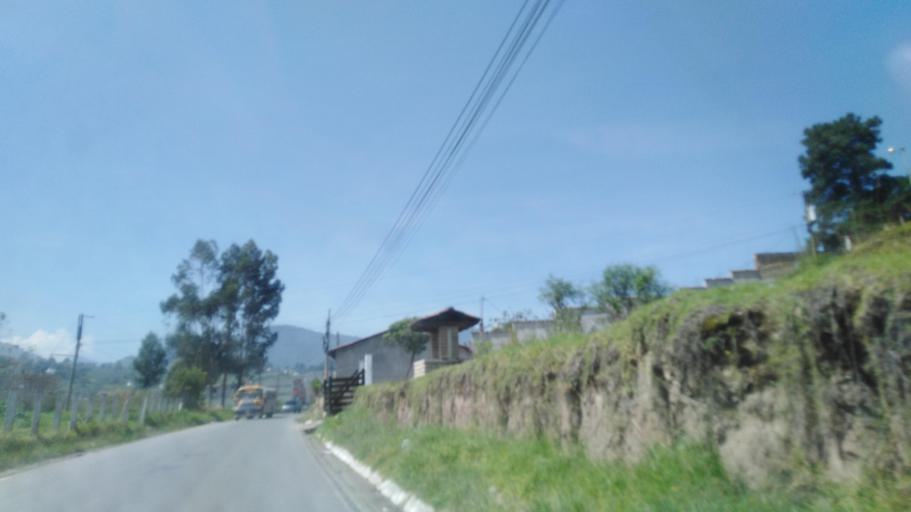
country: GT
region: Quetzaltenango
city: Quetzaltenango
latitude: 14.8573
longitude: -91.4908
